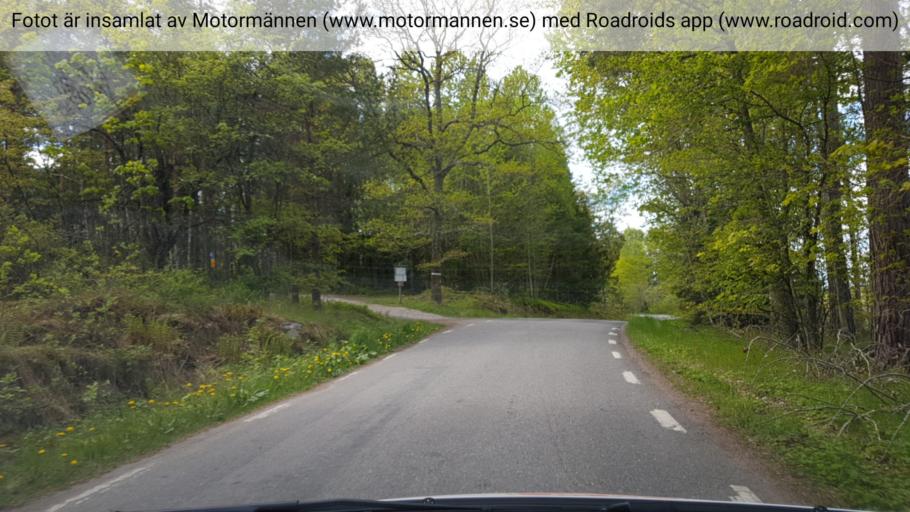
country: SE
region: Kalmar
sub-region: Vasterviks Kommun
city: Forserum
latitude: 57.8569
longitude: 16.5125
